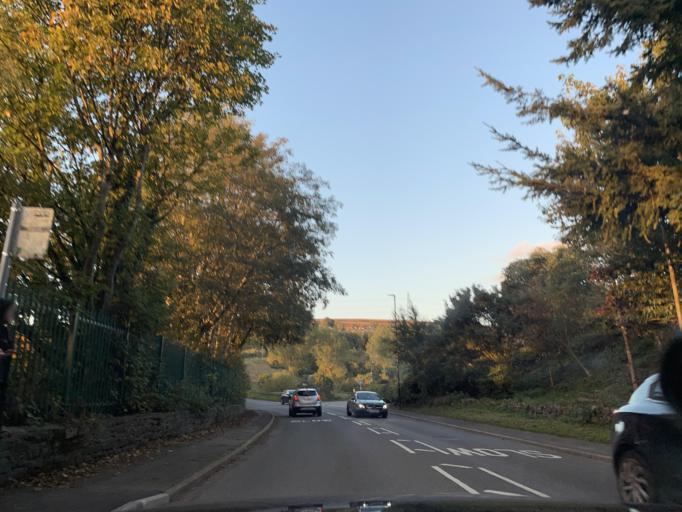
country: GB
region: England
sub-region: Borough of Tameside
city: Longdendale
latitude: 53.4681
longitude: -1.9704
